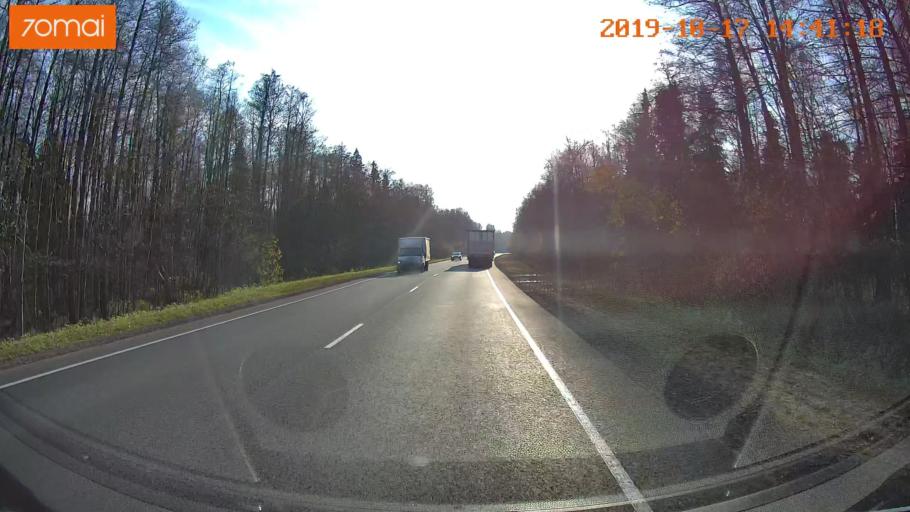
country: RU
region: Rjazan
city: Solotcha
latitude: 54.8466
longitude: 39.9412
